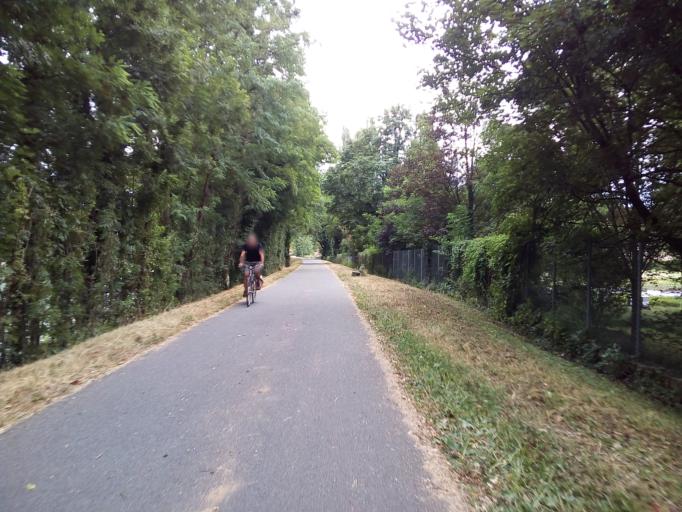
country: FR
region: Rhone-Alpes
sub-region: Departement de l'Isere
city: Corenc
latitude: 45.1960
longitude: 5.7585
